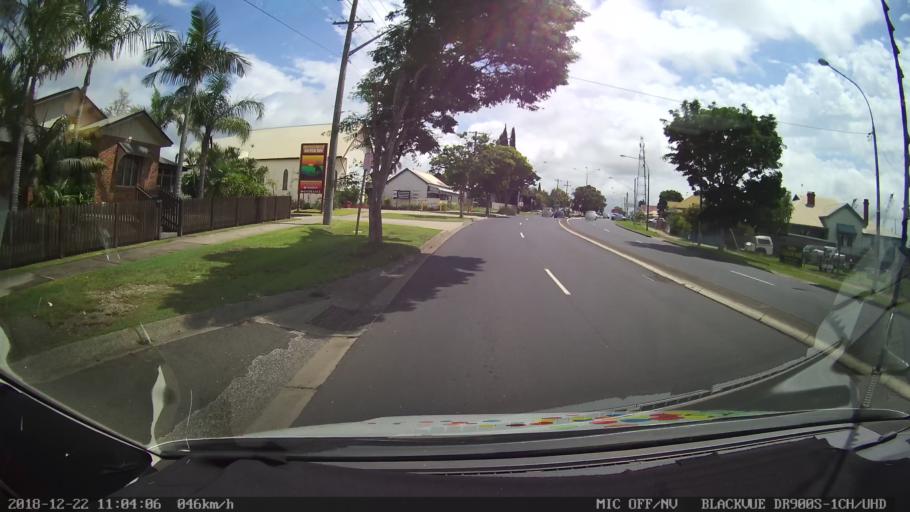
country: AU
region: New South Wales
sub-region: Clarence Valley
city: South Grafton
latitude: -29.7047
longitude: 152.9399
